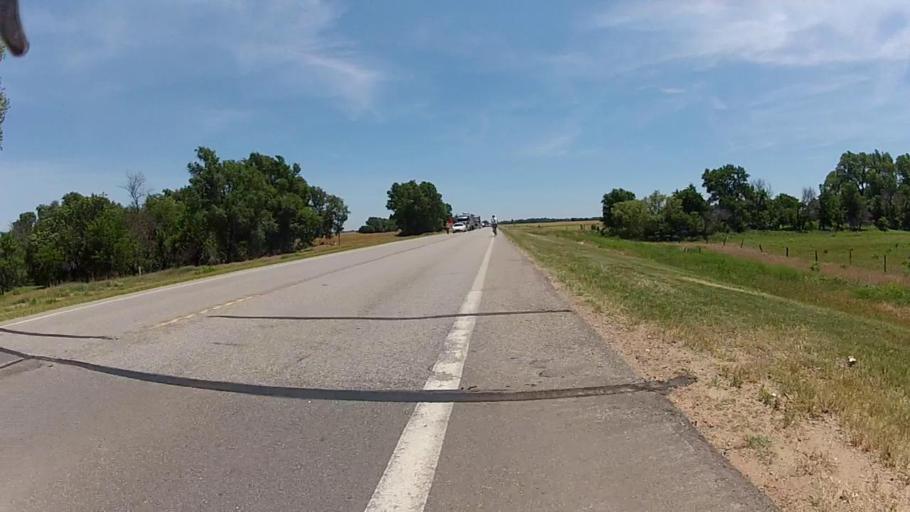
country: US
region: Kansas
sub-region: Barber County
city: Medicine Lodge
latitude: 37.2534
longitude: -98.4527
